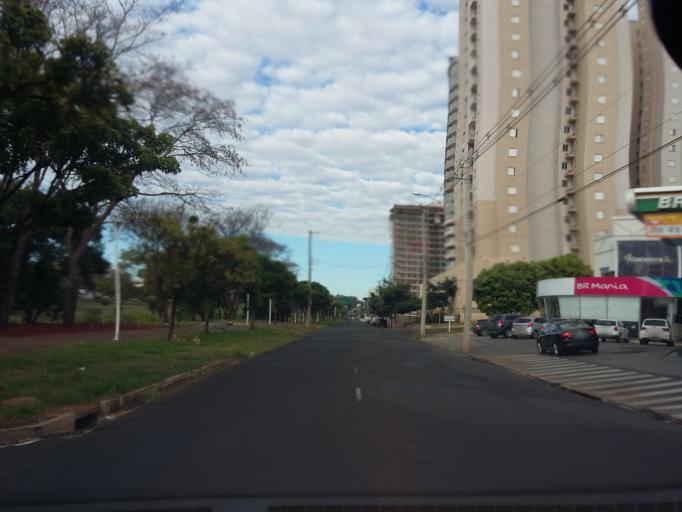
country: BR
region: Sao Paulo
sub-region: Sao Jose Do Rio Preto
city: Sao Jose do Rio Preto
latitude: -20.8362
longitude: -49.4083
